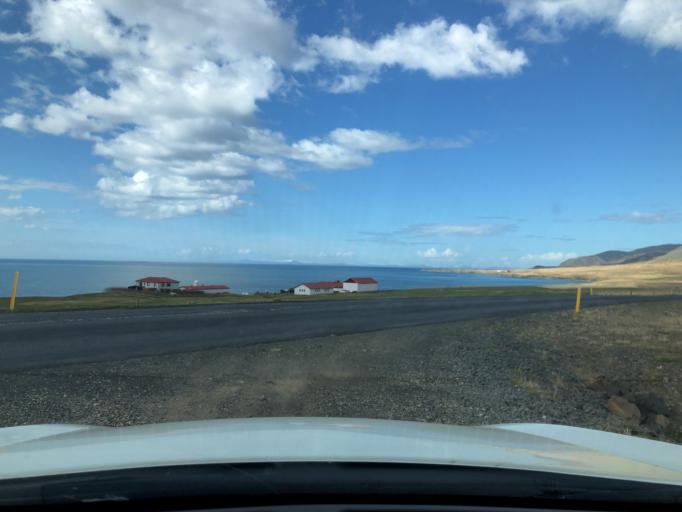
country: IS
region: West
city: Stykkisholmur
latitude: 64.9351
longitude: -23.2042
